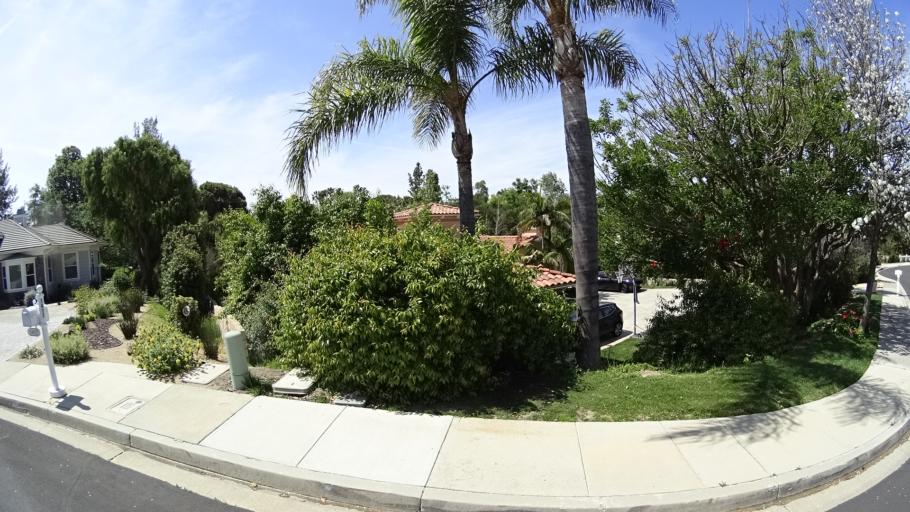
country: US
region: California
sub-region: Ventura County
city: Thousand Oaks
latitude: 34.1972
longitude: -118.8494
